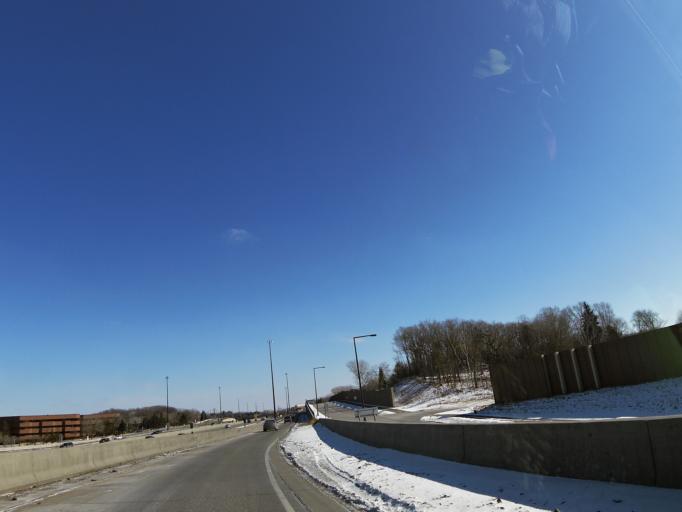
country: US
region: Minnesota
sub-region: Hennepin County
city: Edina
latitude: 44.8587
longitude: -93.3923
